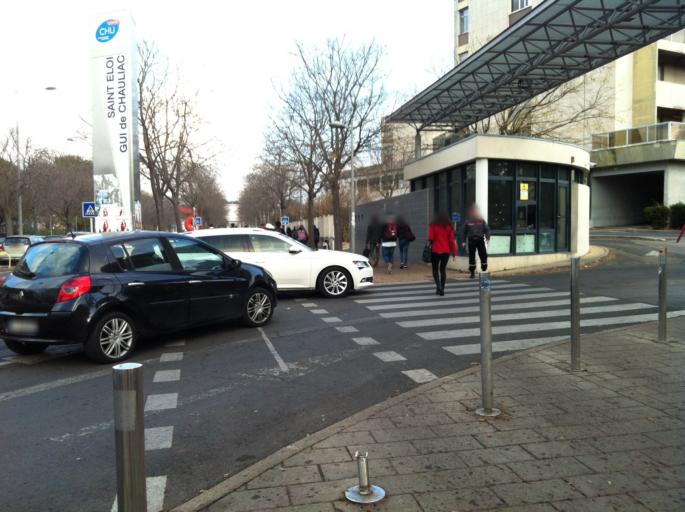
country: FR
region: Languedoc-Roussillon
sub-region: Departement de l'Herault
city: Montpellier
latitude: 43.6295
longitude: 3.8612
